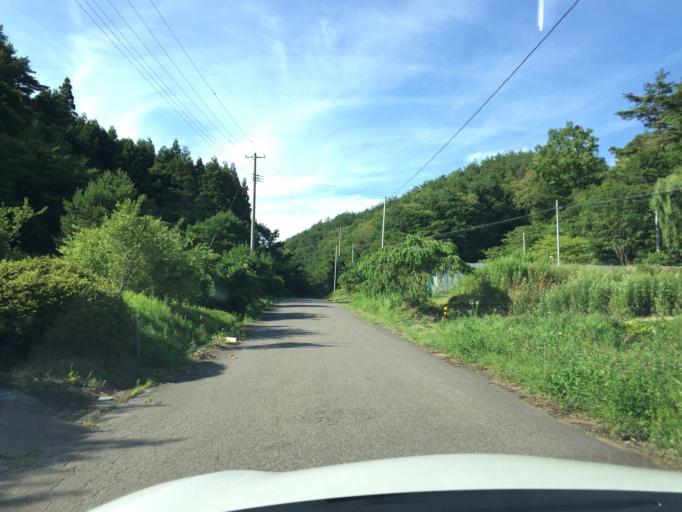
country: JP
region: Fukushima
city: Ishikawa
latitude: 37.2565
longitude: 140.4984
